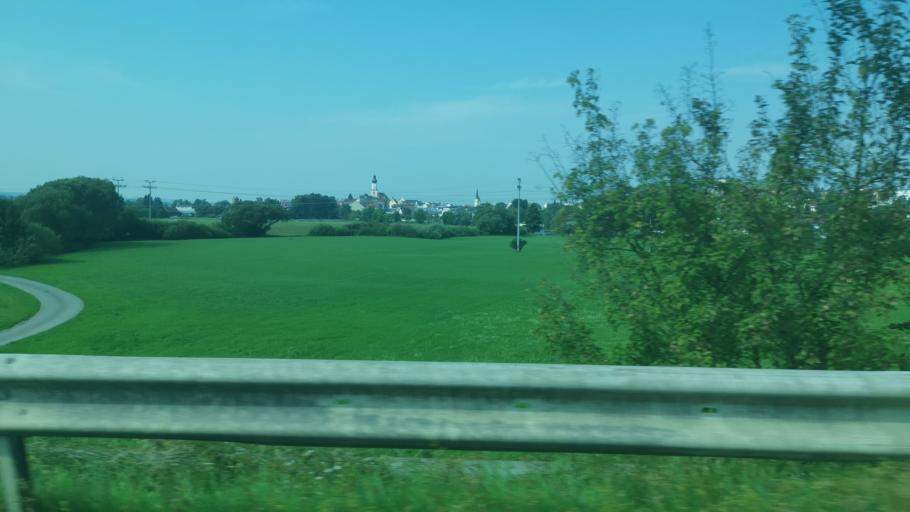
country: DE
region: Bavaria
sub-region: Upper Palatinate
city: Cham
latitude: 49.2203
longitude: 12.6792
